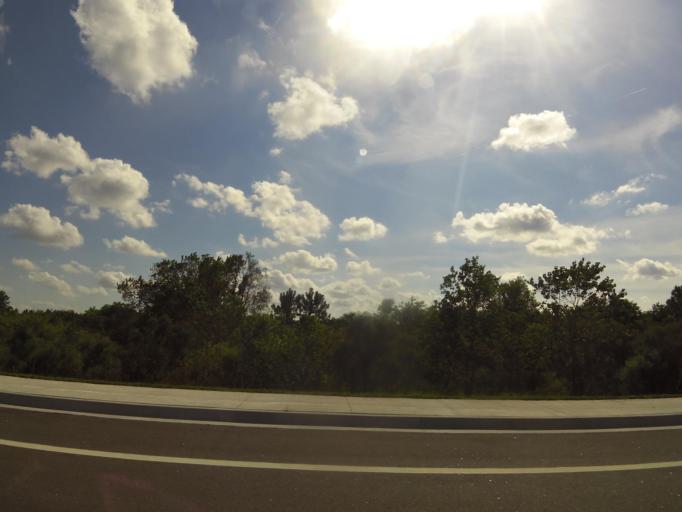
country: US
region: Florida
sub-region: Saint Johns County
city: Villano Beach
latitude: 29.9827
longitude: -81.4657
